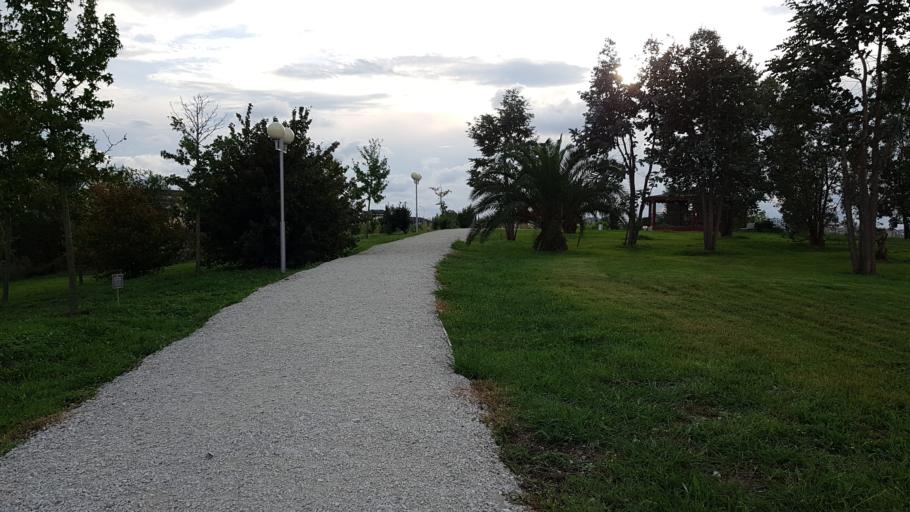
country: RU
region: Krasnodarskiy
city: Vysokoye
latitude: 43.3940
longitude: 39.9909
